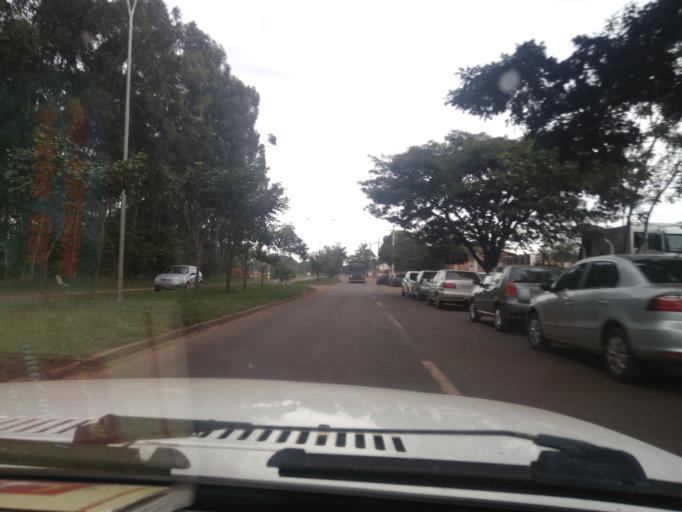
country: BR
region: Mato Grosso do Sul
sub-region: Ponta Pora
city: Ponta Pora
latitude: -22.5201
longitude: -55.7390
